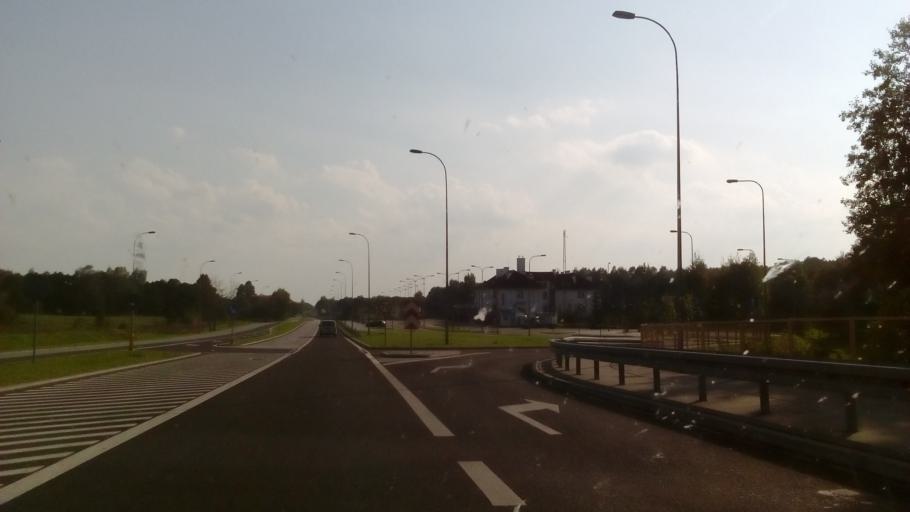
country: LT
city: Lazdijai
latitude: 54.1625
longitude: 23.4748
